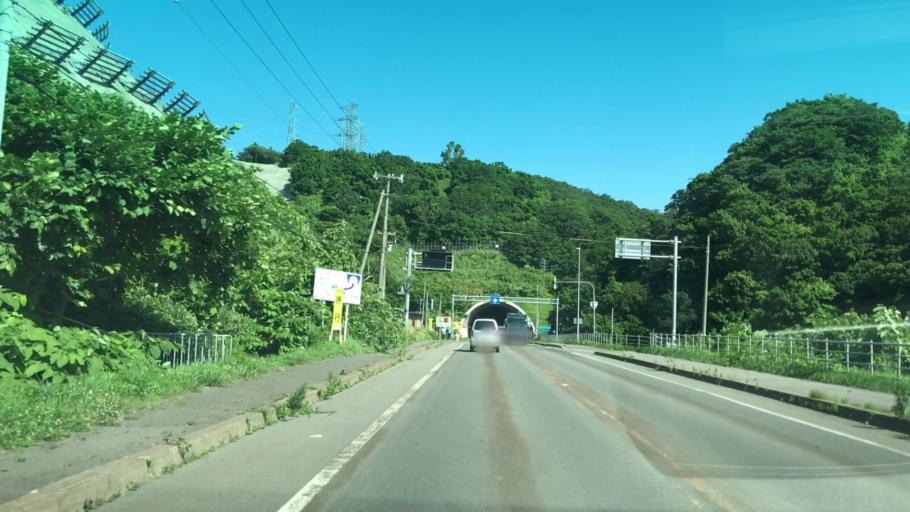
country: JP
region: Hokkaido
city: Iwanai
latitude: 43.0419
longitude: 140.5105
